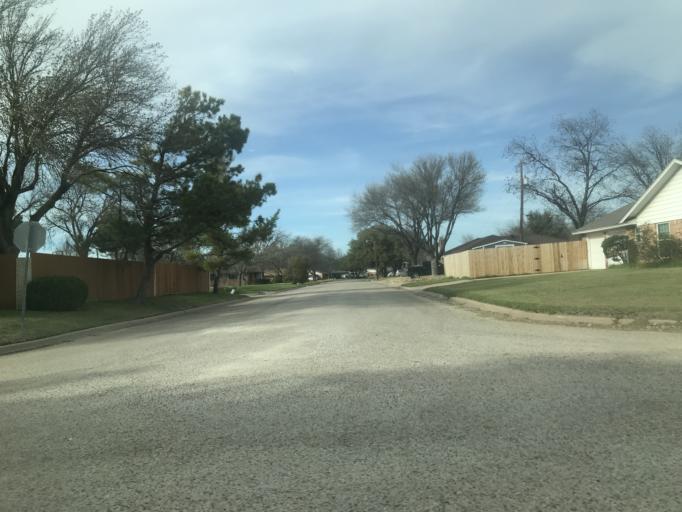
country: US
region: Texas
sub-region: Taylor County
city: Abilene
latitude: 32.4143
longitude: -99.7682
